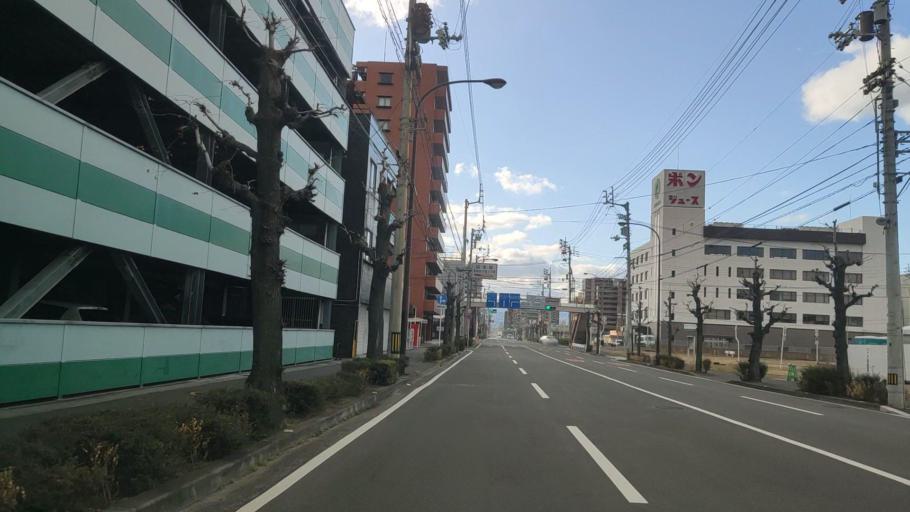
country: JP
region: Ehime
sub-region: Shikoku-chuo Shi
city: Matsuyama
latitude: 33.8382
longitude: 132.7525
